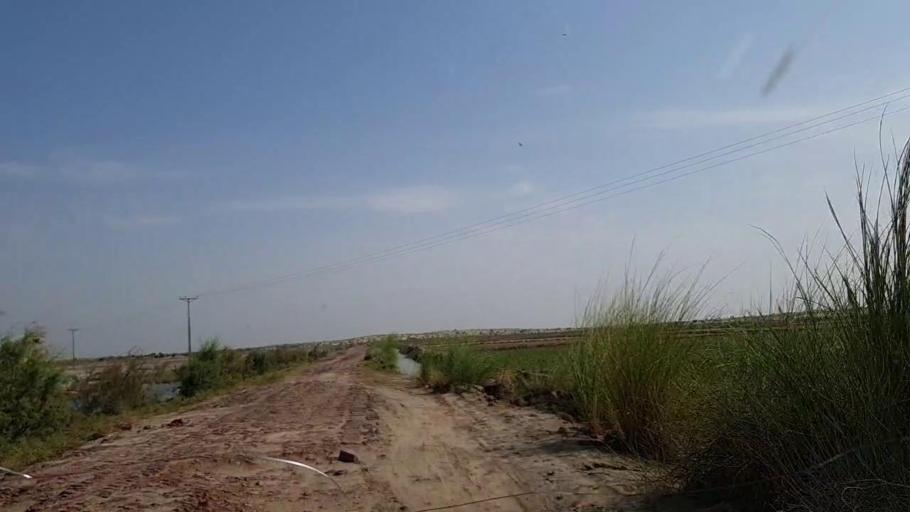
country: PK
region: Sindh
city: Khanpur
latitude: 27.6844
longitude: 69.3679
